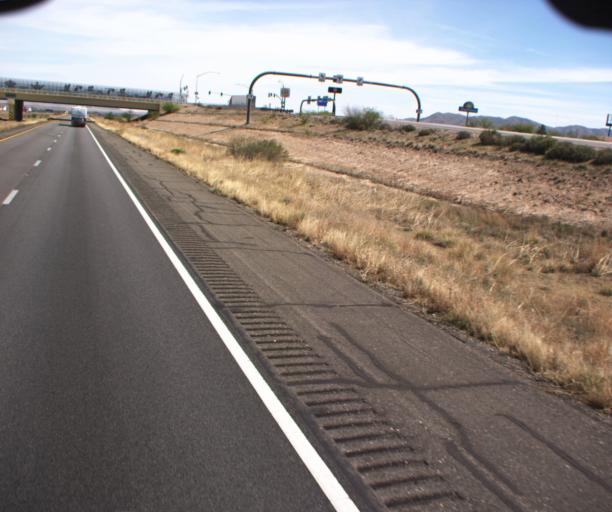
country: US
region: Arizona
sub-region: Cochise County
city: Willcox
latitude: 32.2648
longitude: -109.8450
